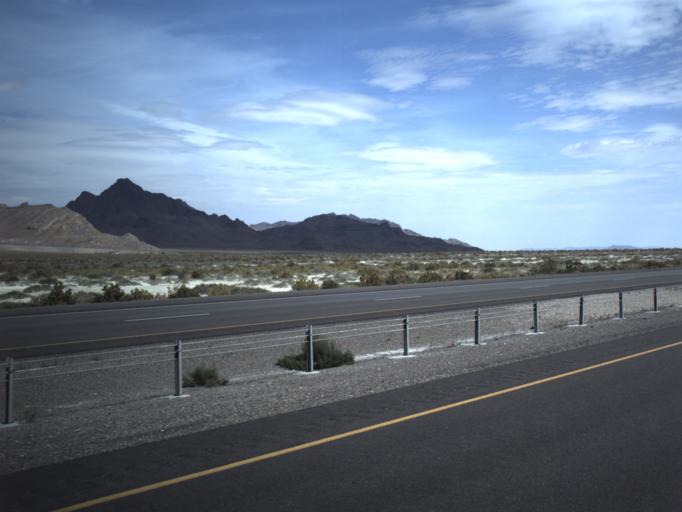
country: US
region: Utah
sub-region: Tooele County
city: Wendover
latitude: 40.7466
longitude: -114.0135
